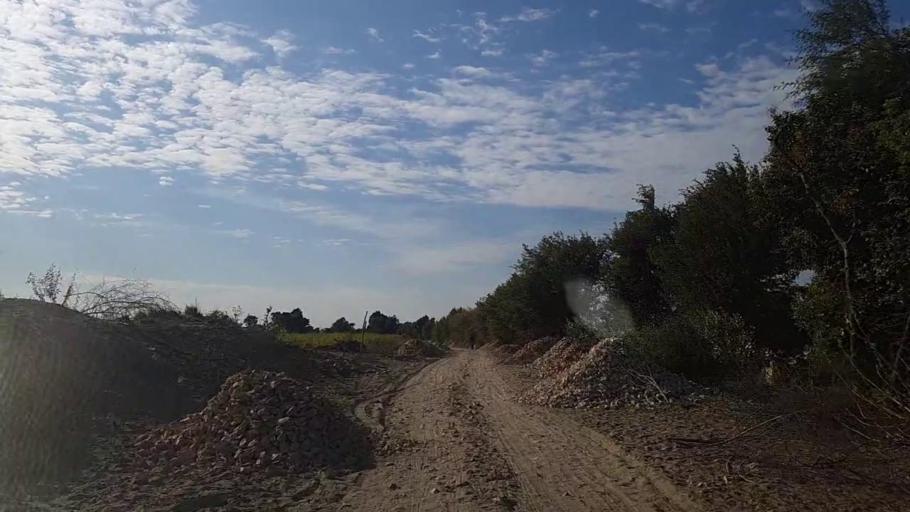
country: PK
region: Sindh
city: Jam Sahib
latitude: 26.3138
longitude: 68.8104
